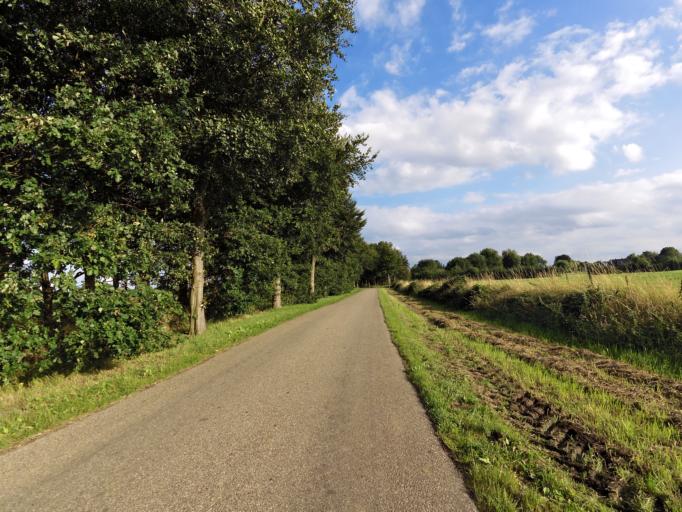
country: NL
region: Gelderland
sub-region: Gemeente Doesburg
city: Doesburg
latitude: 51.9897
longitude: 6.1167
